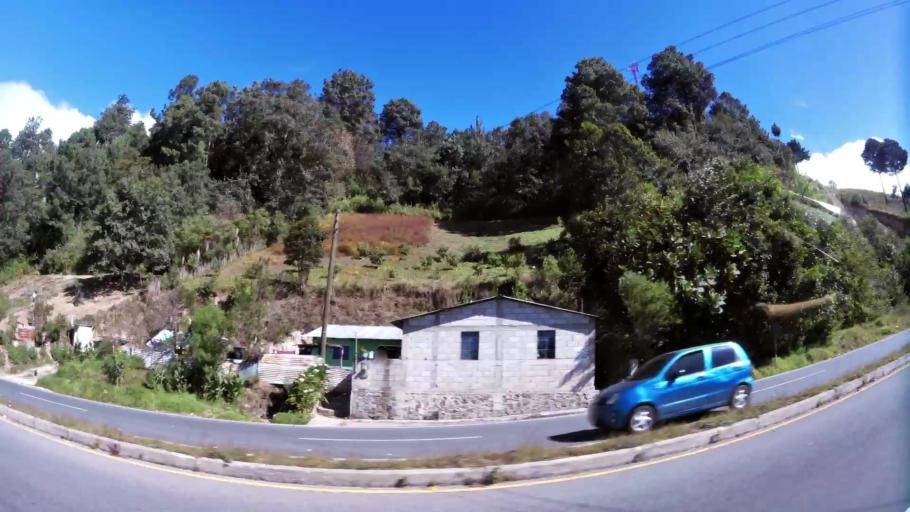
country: GT
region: Solola
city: Solola
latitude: 14.8280
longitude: -91.1870
